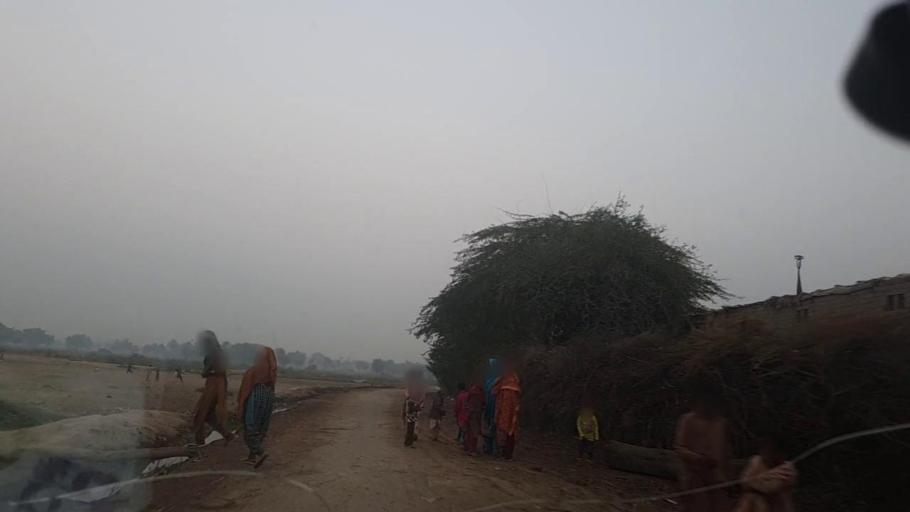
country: PK
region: Sindh
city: Hingorja
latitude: 27.2205
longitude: 68.4283
